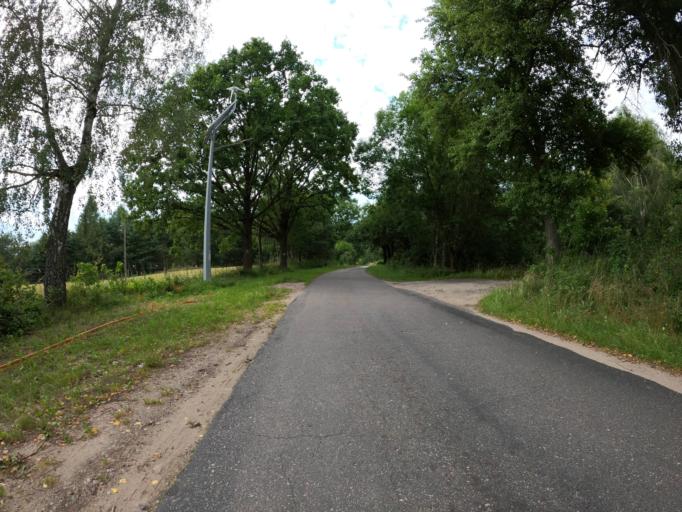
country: PL
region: West Pomeranian Voivodeship
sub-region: Powiat szczecinecki
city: Borne Sulinowo
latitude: 53.6296
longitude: 16.5556
